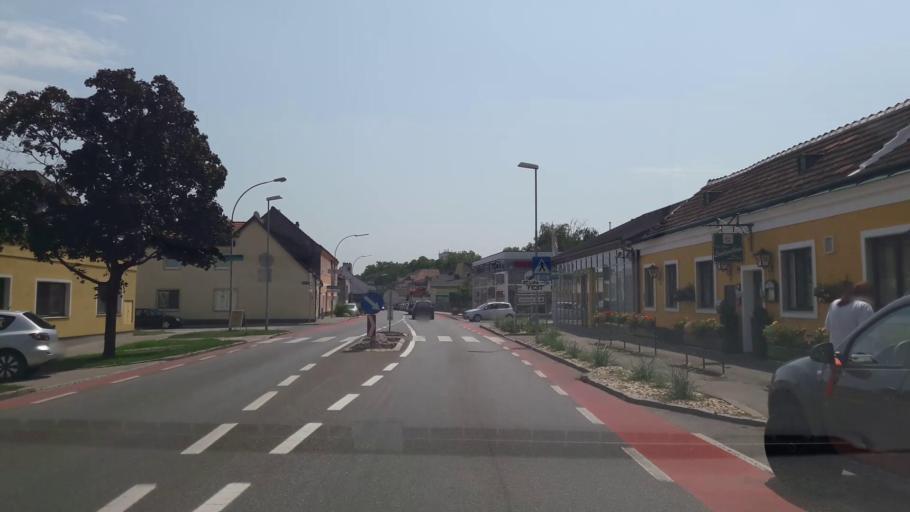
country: AT
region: Lower Austria
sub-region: Politischer Bezirk Wien-Umgebung
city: Schwadorf
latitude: 48.0723
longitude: 16.5810
